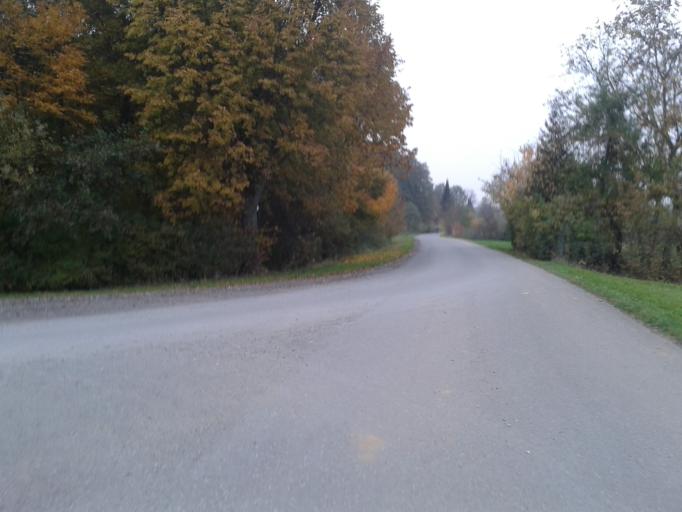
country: DE
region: Bavaria
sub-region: Upper Franconia
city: Gundelsheim
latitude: 49.9285
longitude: 10.9377
